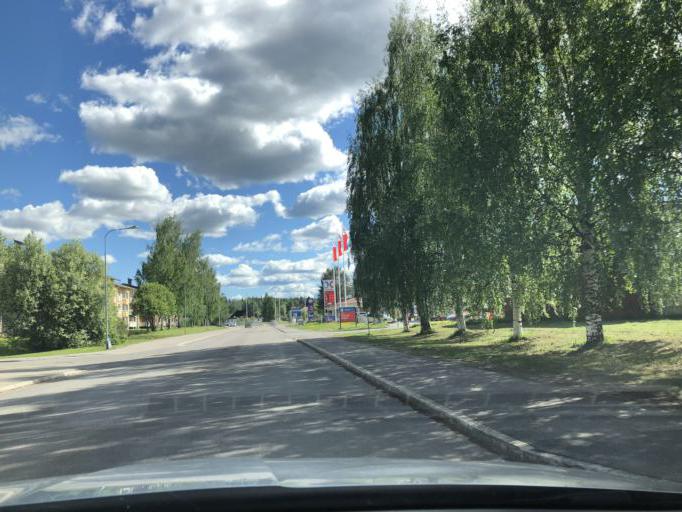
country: SE
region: Norrbotten
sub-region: Alvsbyns Kommun
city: AElvsbyn
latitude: 65.6737
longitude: 21.0057
